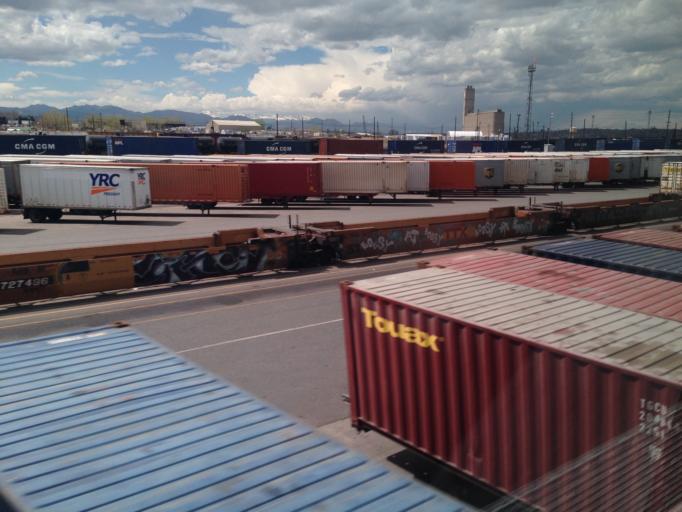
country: US
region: Colorado
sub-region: Adams County
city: Twin Lakes
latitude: 39.7959
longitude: -104.9968
